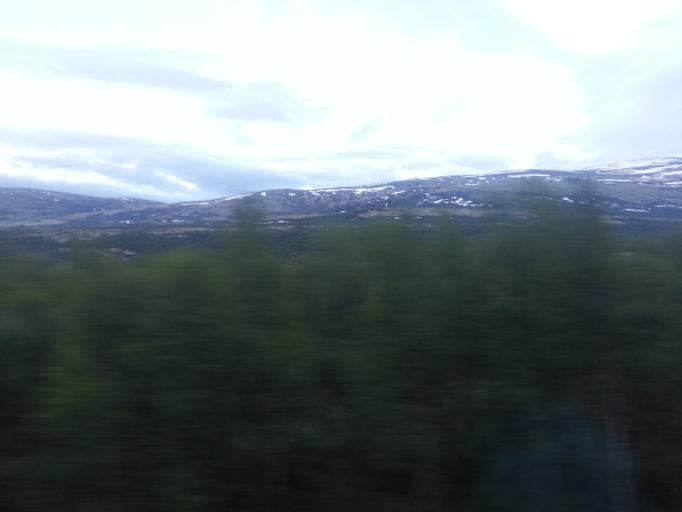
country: NO
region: Oppland
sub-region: Dovre
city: Dovre
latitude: 62.1955
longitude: 9.4985
